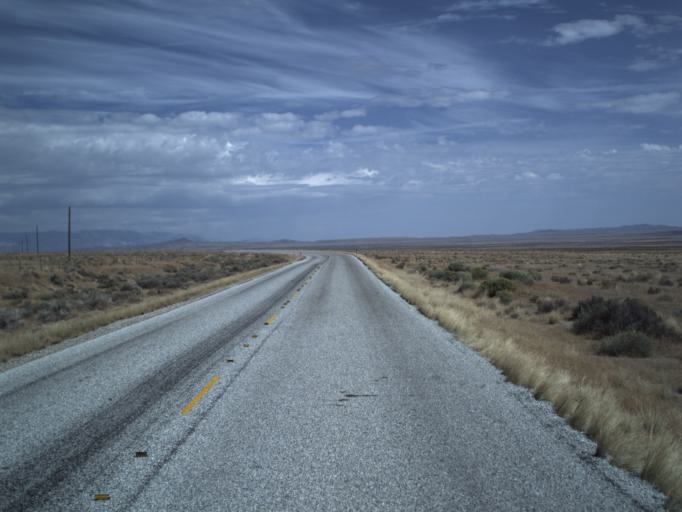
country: US
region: Utah
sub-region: Tooele County
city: Wendover
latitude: 41.5028
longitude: -113.6054
